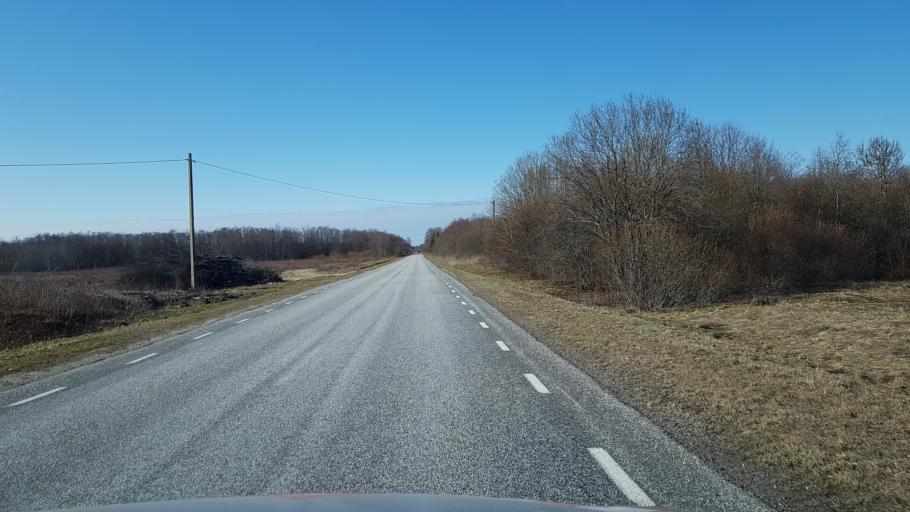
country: EE
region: Laeaene-Virumaa
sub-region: Haljala vald
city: Haljala
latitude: 59.4871
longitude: 26.1495
